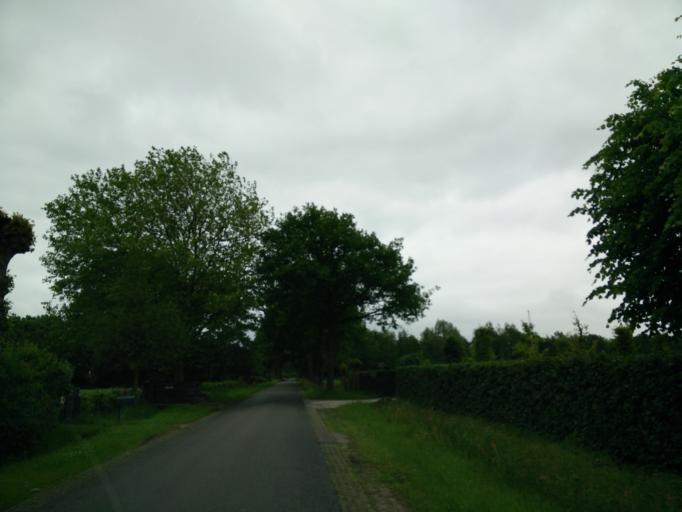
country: NL
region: Groningen
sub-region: Gemeente Leek
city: Leek
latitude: 53.1408
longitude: 6.4748
